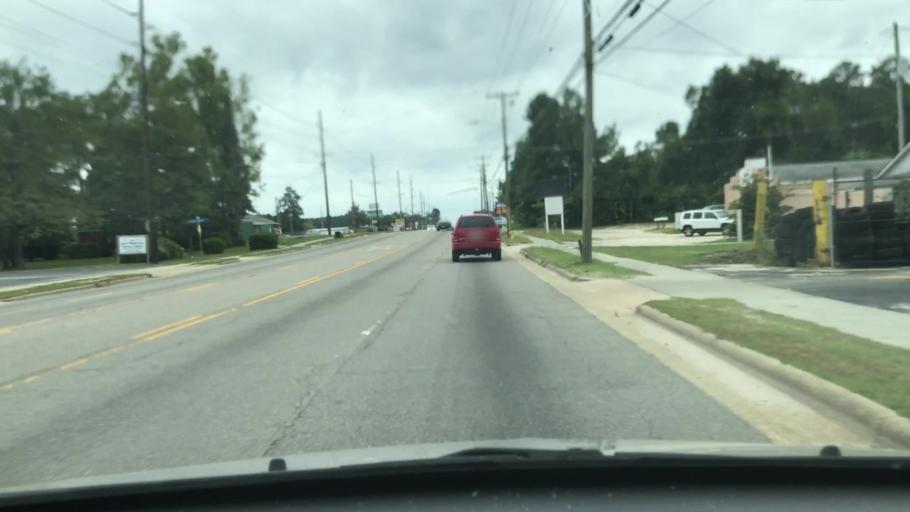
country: US
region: North Carolina
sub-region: Cumberland County
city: Fayetteville
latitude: 35.1013
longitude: -78.9193
